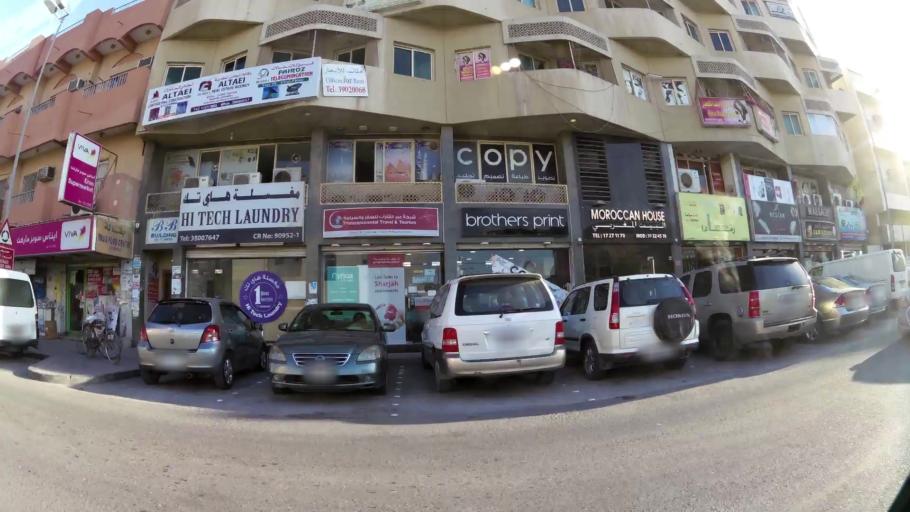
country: BH
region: Manama
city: Manama
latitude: 26.2297
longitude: 50.5940
